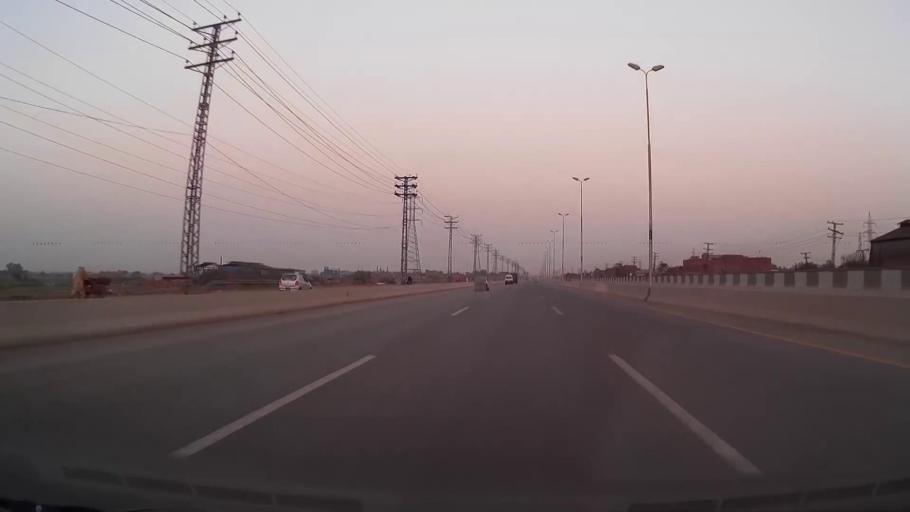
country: PK
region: Punjab
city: Lahore
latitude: 31.6095
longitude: 74.3286
